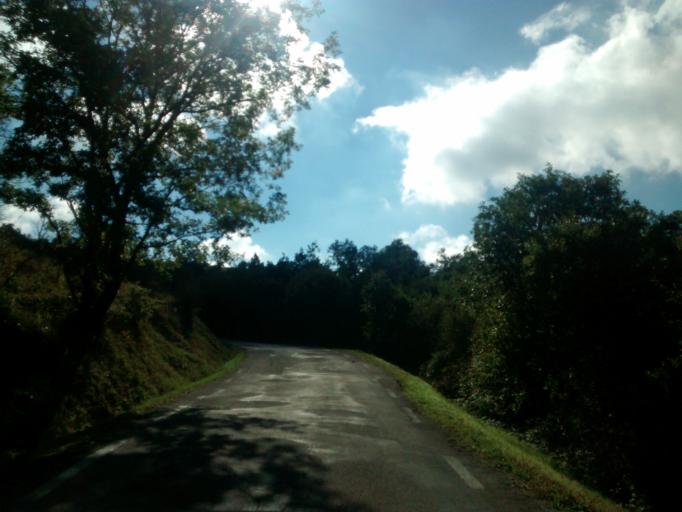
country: ES
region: Castille and Leon
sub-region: Provincia de Burgos
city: Arija
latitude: 42.9300
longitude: -4.0119
